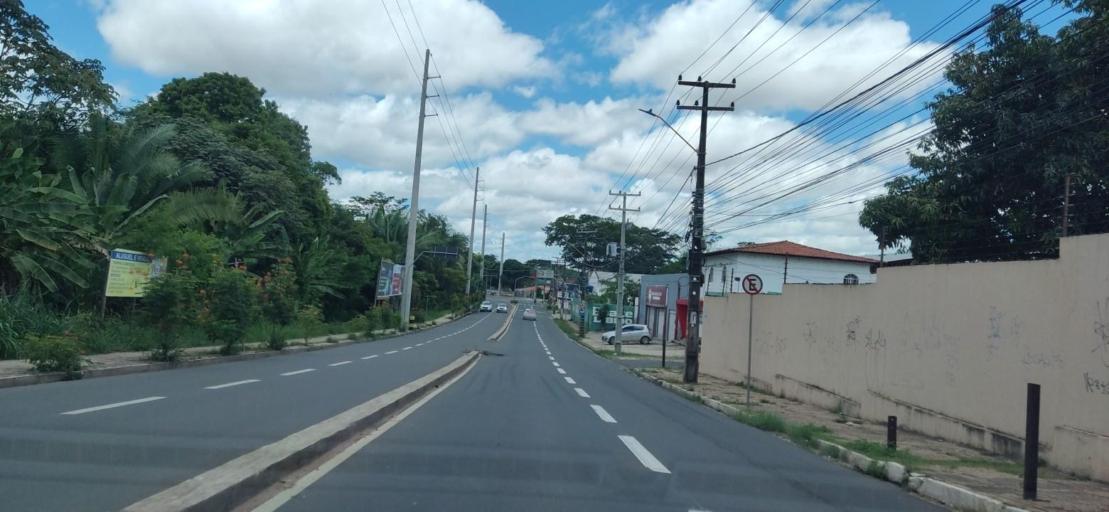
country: BR
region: Piaui
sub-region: Teresina
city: Teresina
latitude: -5.0844
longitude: -42.7658
